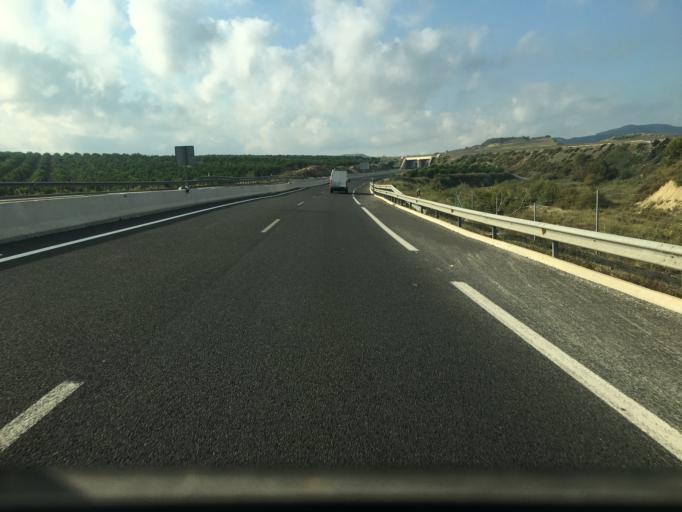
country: ES
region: Murcia
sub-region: Murcia
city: Beniel
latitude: 37.9915
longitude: -0.9753
